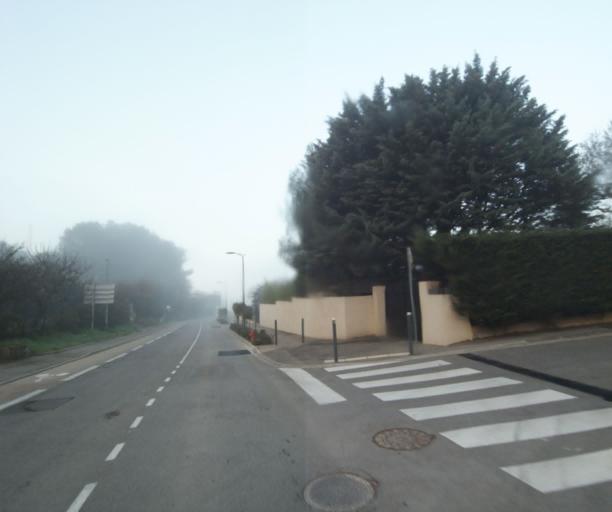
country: FR
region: Provence-Alpes-Cote d'Azur
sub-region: Departement des Bouches-du-Rhone
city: Meyreuil
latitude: 43.4815
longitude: 5.4964
